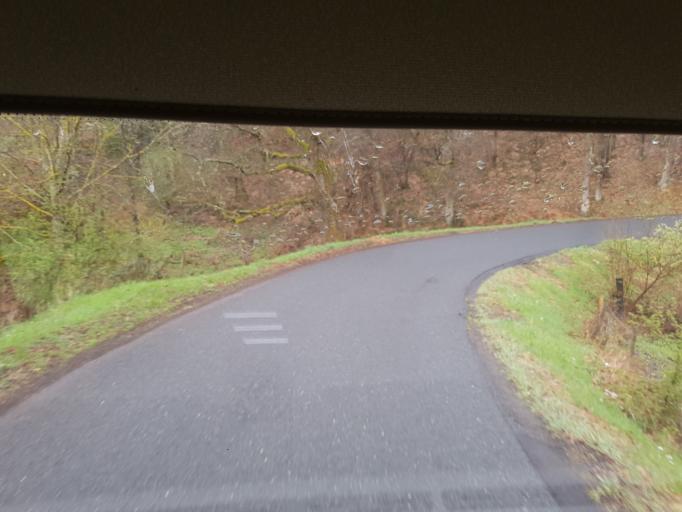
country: FR
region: Rhone-Alpes
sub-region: Departement de la Loire
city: Le Chambon-Feugerolles
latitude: 45.4112
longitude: 4.3314
